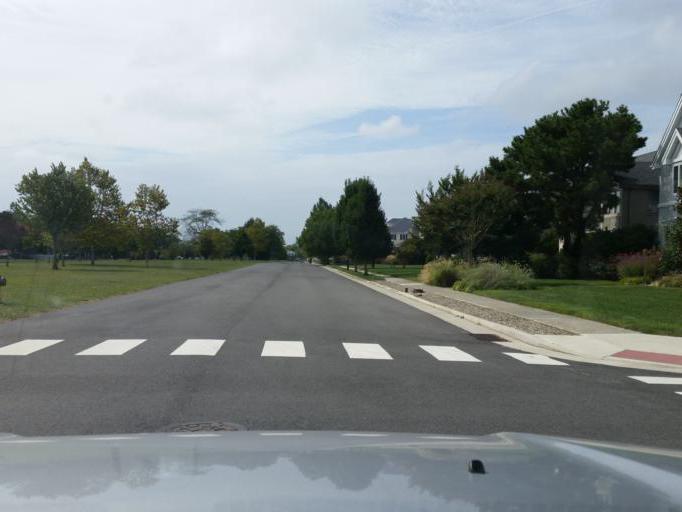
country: US
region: New Jersey
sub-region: Cape May County
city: Cape May
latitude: 38.9380
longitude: -74.9080
